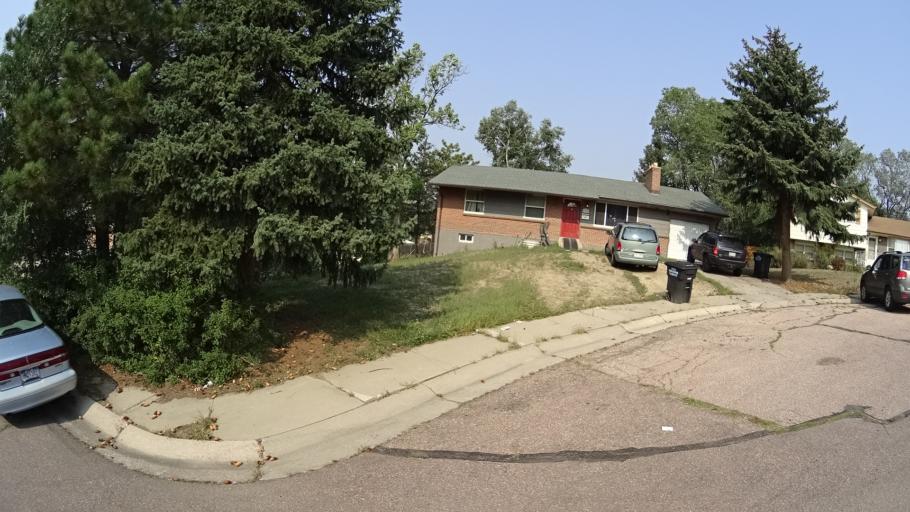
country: US
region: Colorado
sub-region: El Paso County
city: Stratmoor
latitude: 38.8128
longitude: -104.7718
